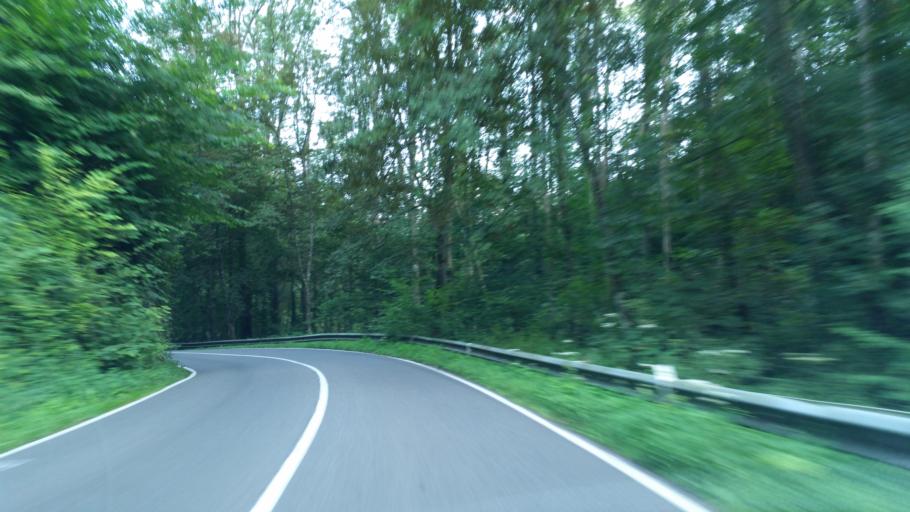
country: BE
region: Wallonia
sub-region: Province du Luxembourg
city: Durbuy
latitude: 50.3621
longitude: 5.4542
